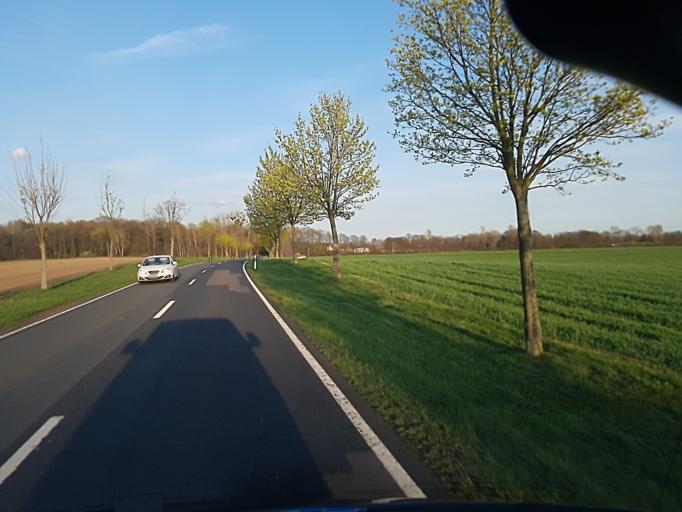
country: DE
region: Saxony
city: Trossin
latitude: 51.5656
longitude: 12.8663
